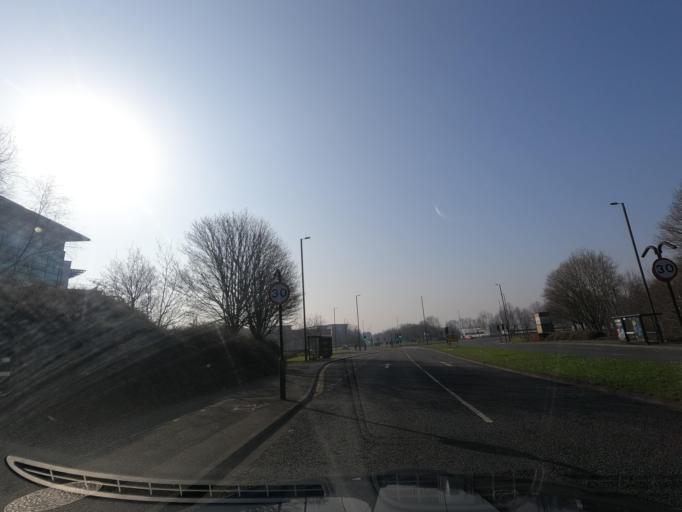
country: GB
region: England
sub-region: Newcastle upon Tyne
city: Gosforth
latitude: 55.0209
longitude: -1.5845
